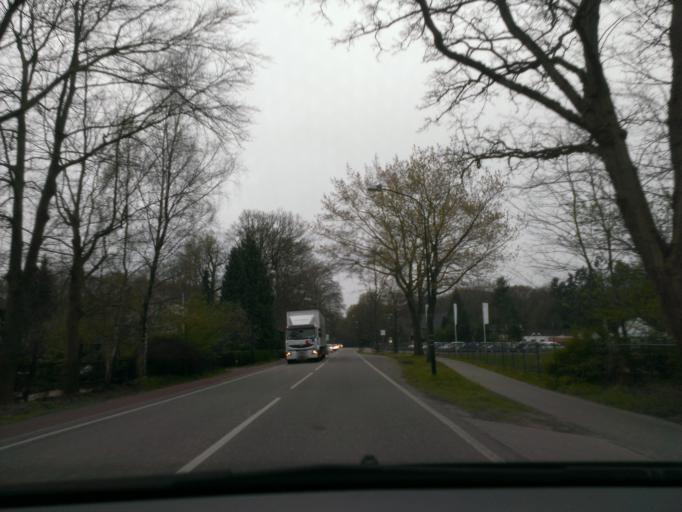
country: NL
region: Gelderland
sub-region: Gemeente Epe
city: Vaassen
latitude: 52.2606
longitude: 5.9535
